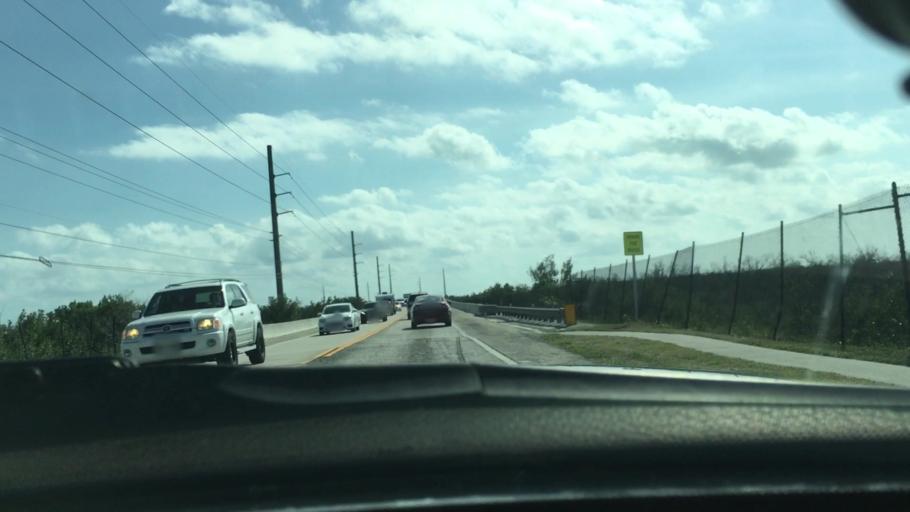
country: US
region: Florida
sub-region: Monroe County
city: Big Pine Key
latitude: 24.6555
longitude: -81.3360
